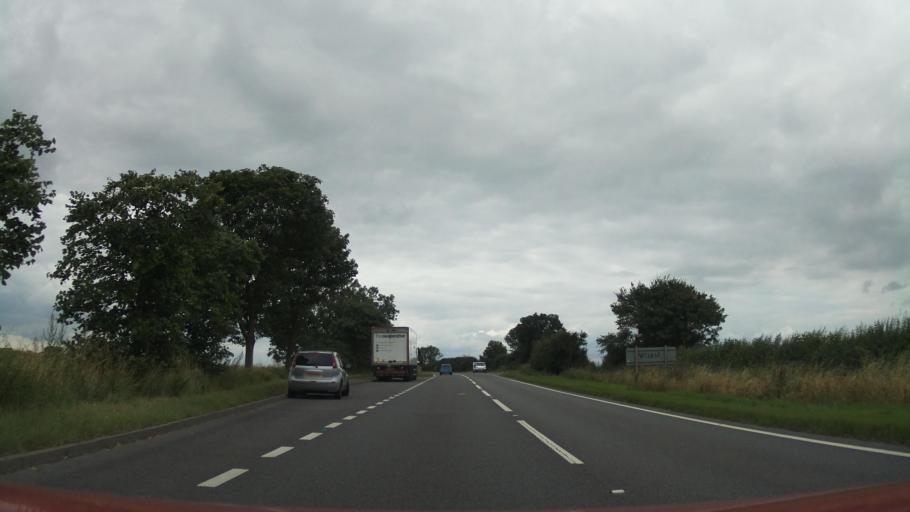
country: GB
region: England
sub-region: Lincolnshire
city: Barrowby
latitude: 52.9316
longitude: -0.7406
